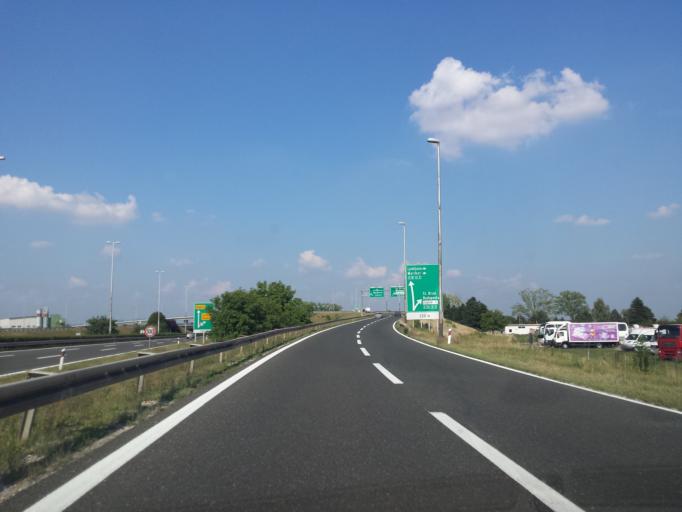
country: HR
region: Grad Zagreb
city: Lucko
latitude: 45.7551
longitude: 15.8919
